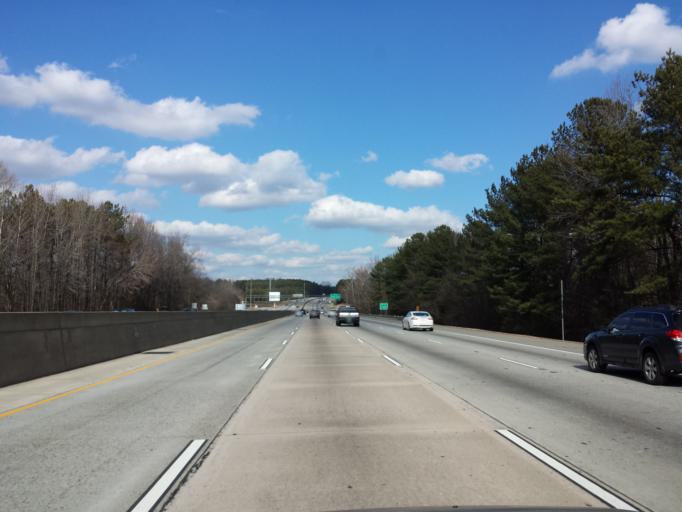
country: US
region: Georgia
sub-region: Fulton County
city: Roswell
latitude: 34.0319
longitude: -84.3170
